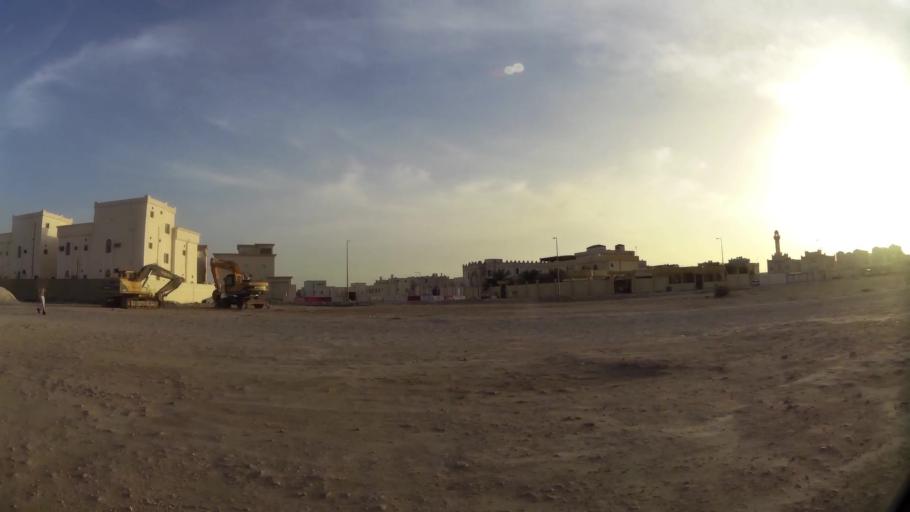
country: QA
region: Al Wakrah
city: Al Wakrah
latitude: 25.1485
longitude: 51.6082
